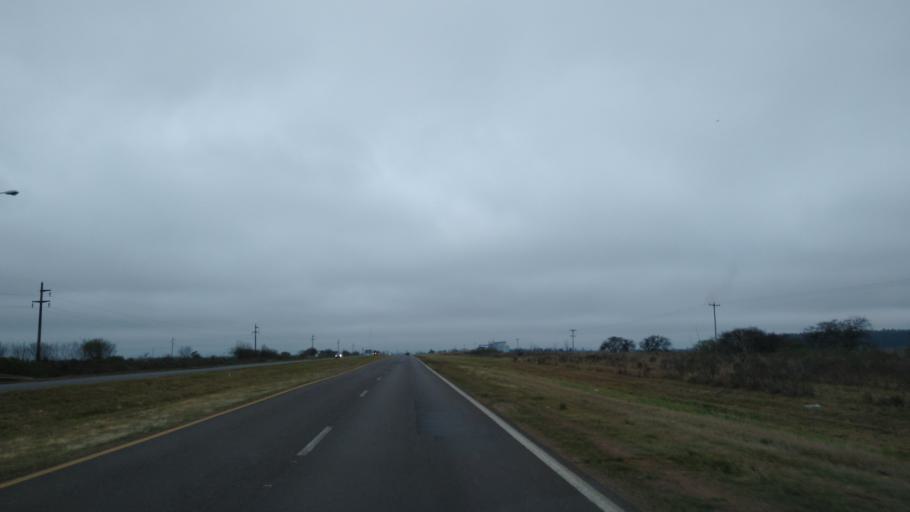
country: AR
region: Entre Rios
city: Chajari
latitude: -30.7964
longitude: -58.0326
